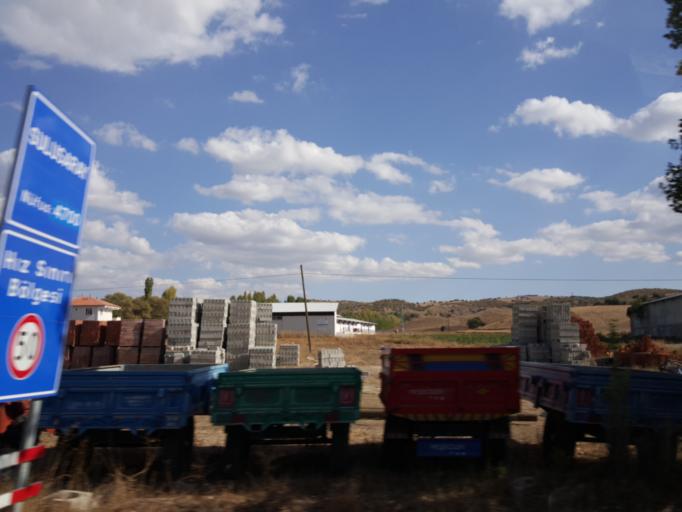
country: TR
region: Tokat
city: Sulusaray
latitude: 39.9790
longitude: 36.0595
